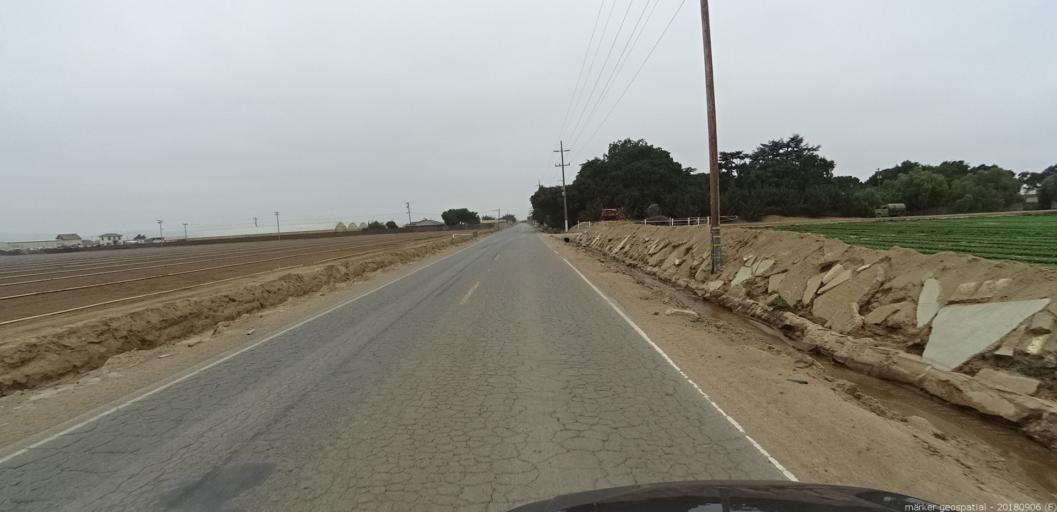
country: US
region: California
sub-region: Monterey County
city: Chualar
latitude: 36.6370
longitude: -121.5603
